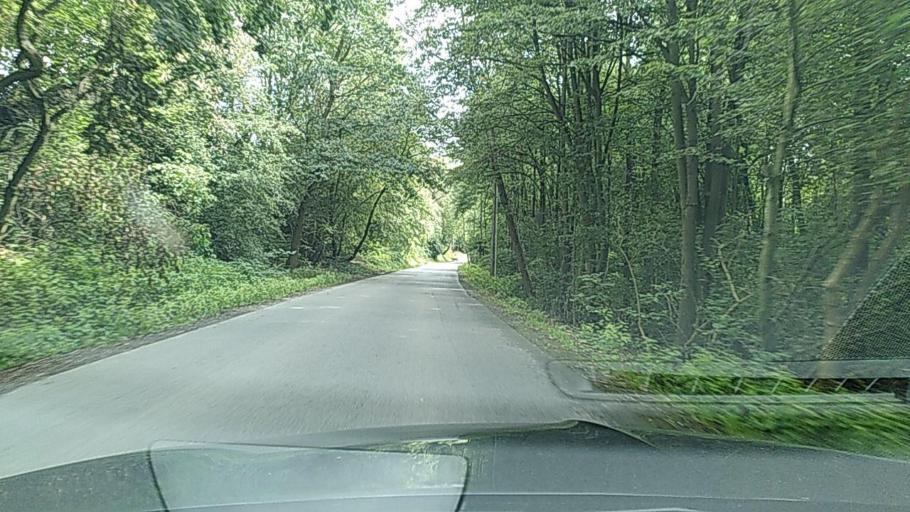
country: PL
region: Lesser Poland Voivodeship
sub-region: Powiat krakowski
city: Rzaska
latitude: 50.0912
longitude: 19.8692
